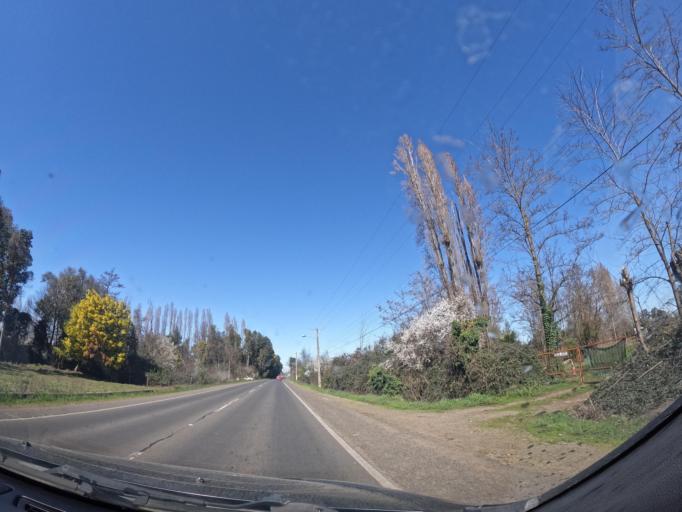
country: CL
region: Maule
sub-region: Provincia de Linares
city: Parral
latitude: -36.1507
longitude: -71.7505
